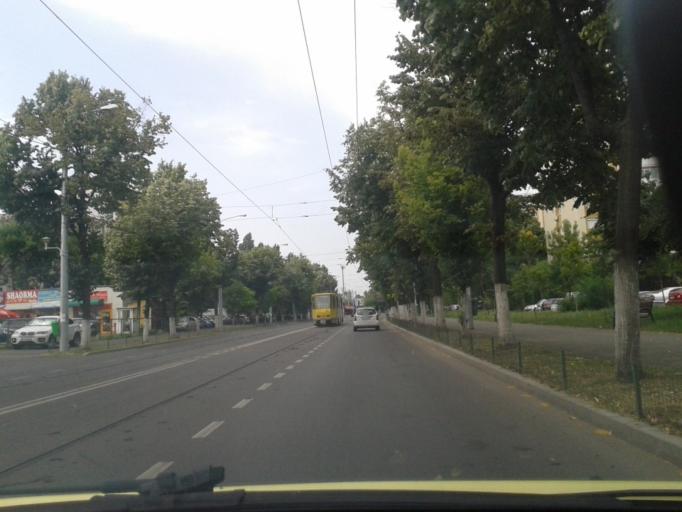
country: RO
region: Prahova
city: Ploiesti
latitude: 44.9447
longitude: 25.9933
